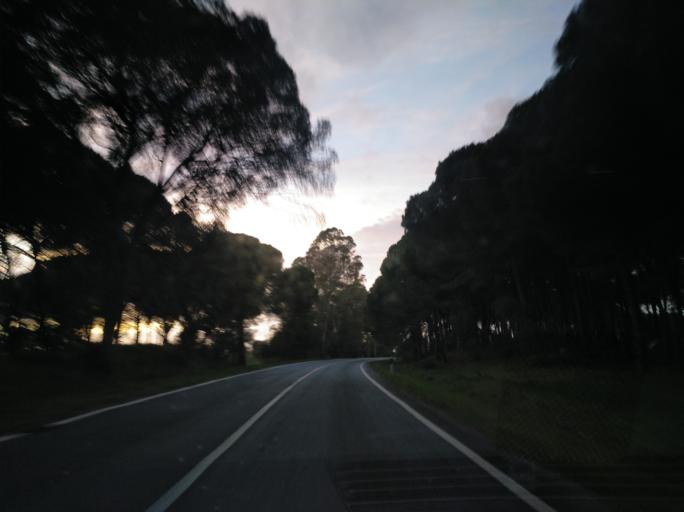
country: PT
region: Setubal
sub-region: Grandola
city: Grandola
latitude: 38.2009
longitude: -8.6218
